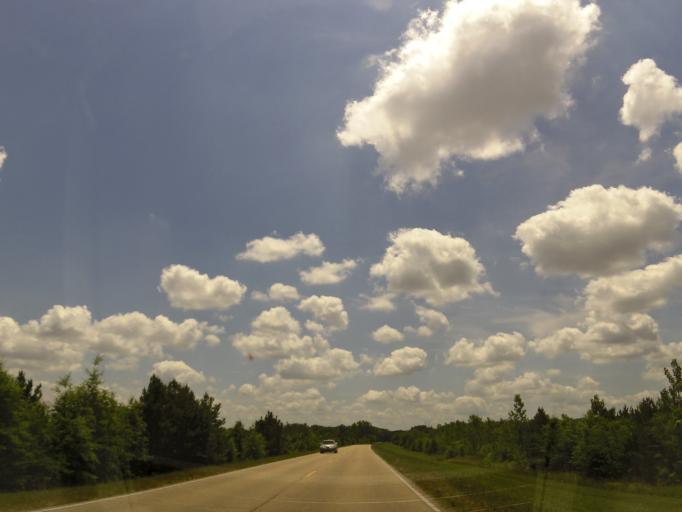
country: US
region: Mississippi
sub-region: Lee County
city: Tupelo
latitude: 34.3134
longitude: -88.7182
